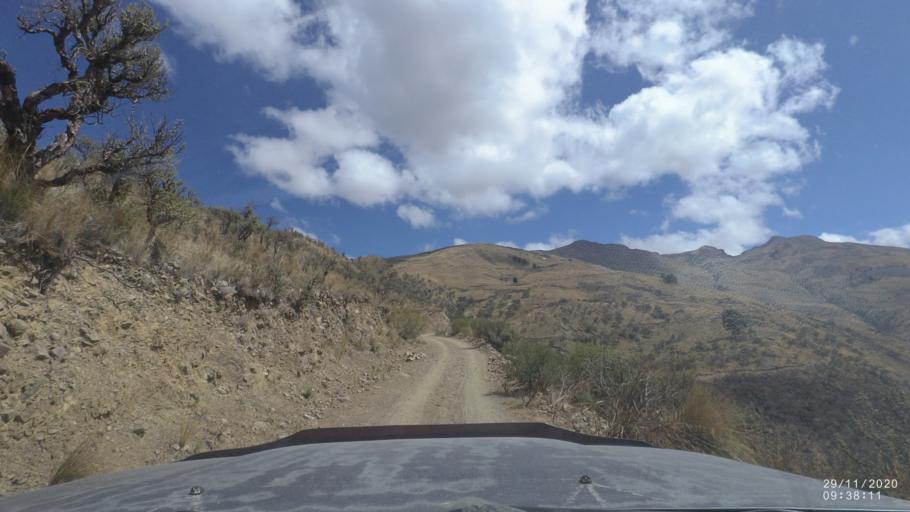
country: BO
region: Cochabamba
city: Cochabamba
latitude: -17.3084
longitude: -66.1846
